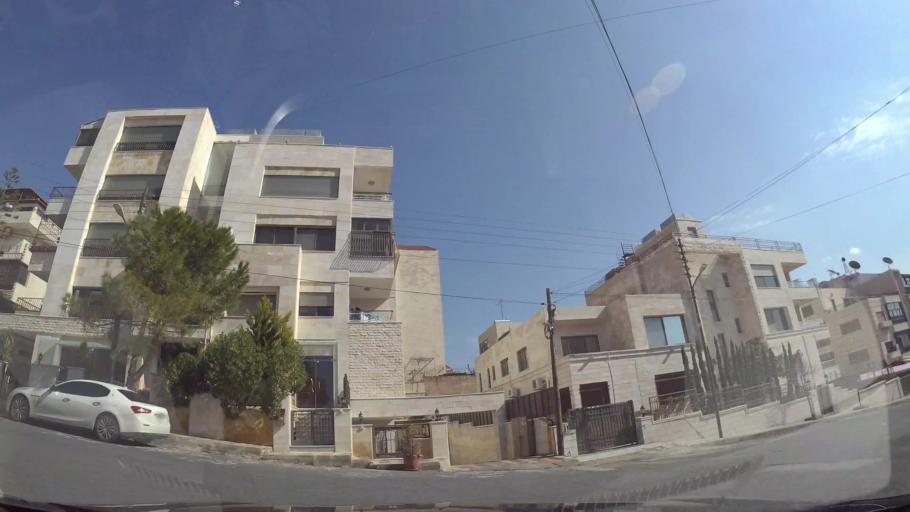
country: JO
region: Amman
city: Al Jubayhah
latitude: 31.9972
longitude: 35.8901
